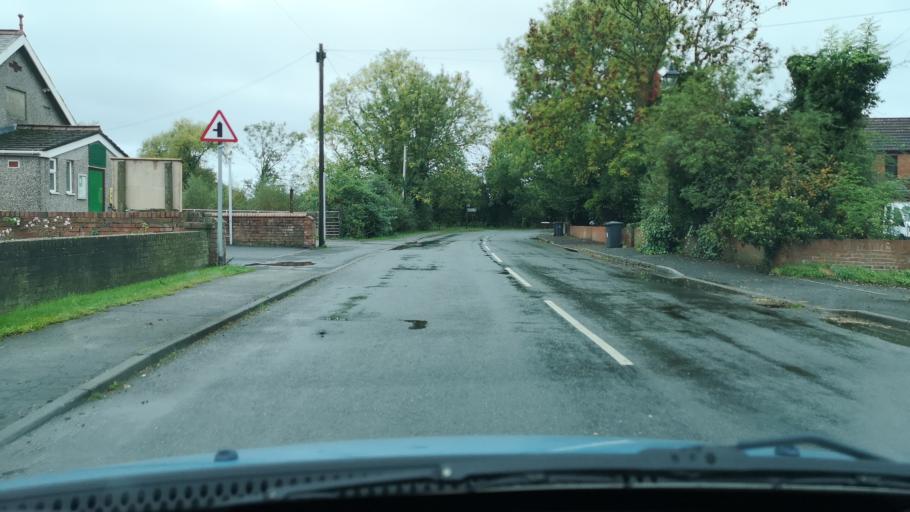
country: GB
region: England
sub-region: Doncaster
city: Stainforth
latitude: 53.6116
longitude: -1.0111
